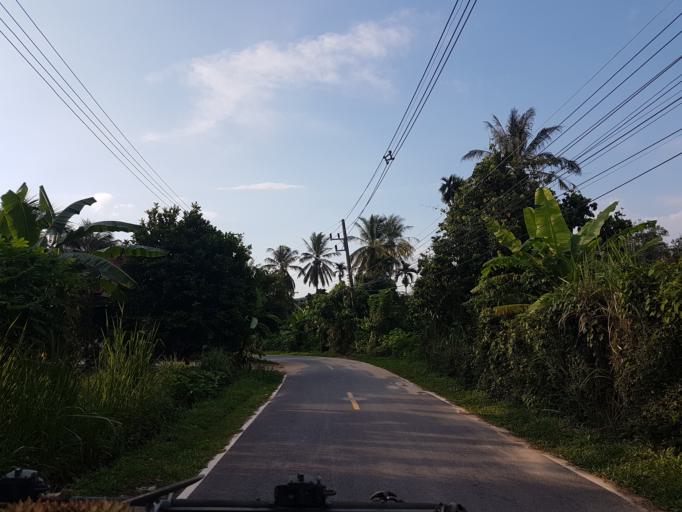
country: TH
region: Pattani
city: Khok Pho
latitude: 6.6745
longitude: 101.0949
